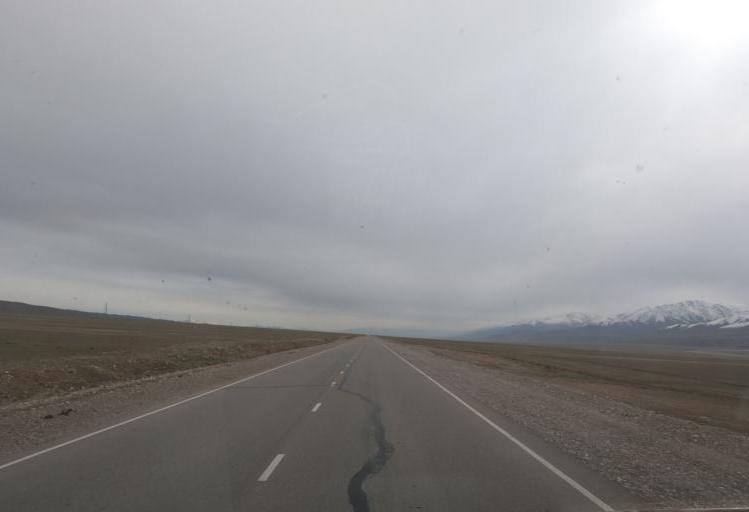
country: KG
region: Naryn
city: Baetov
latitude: 40.9660
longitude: 75.3008
